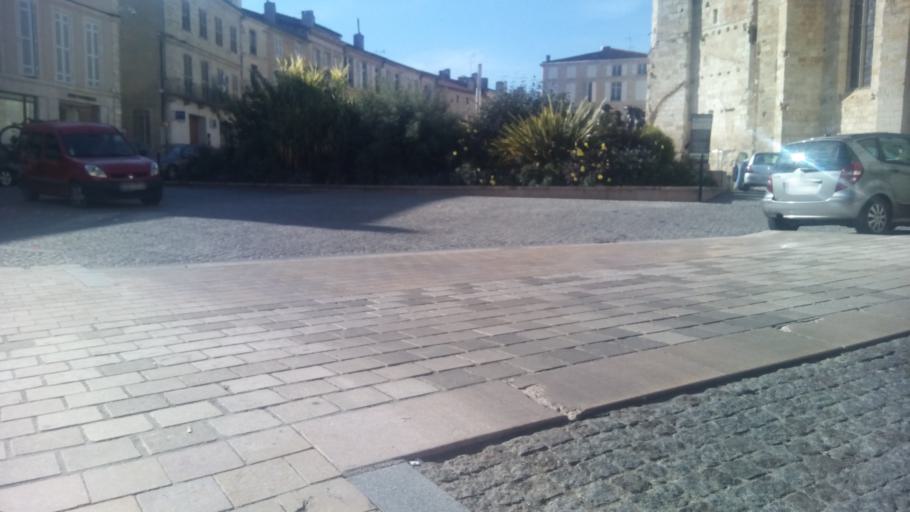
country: FR
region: Midi-Pyrenees
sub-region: Departement du Gers
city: Condom
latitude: 43.9573
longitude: 0.3741
